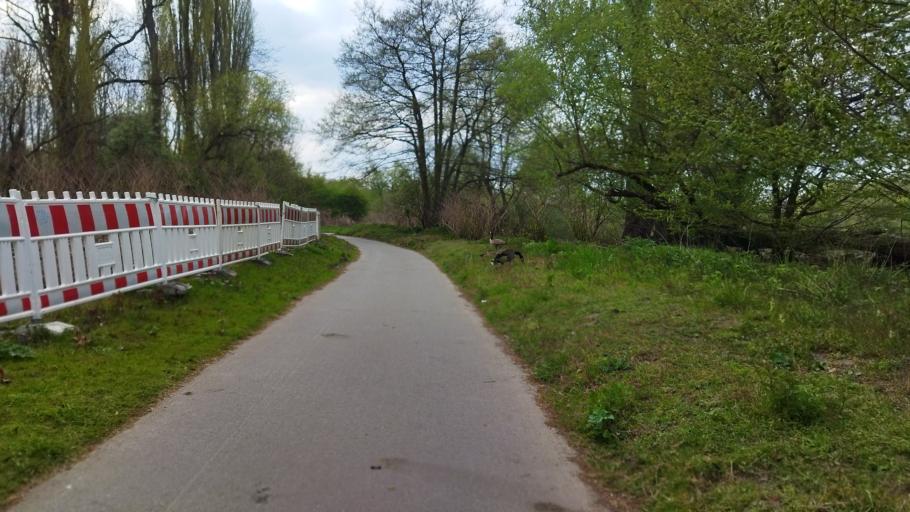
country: DE
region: North Rhine-Westphalia
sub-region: Regierungsbezirk Dusseldorf
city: Essen
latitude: 51.4207
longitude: 7.0657
